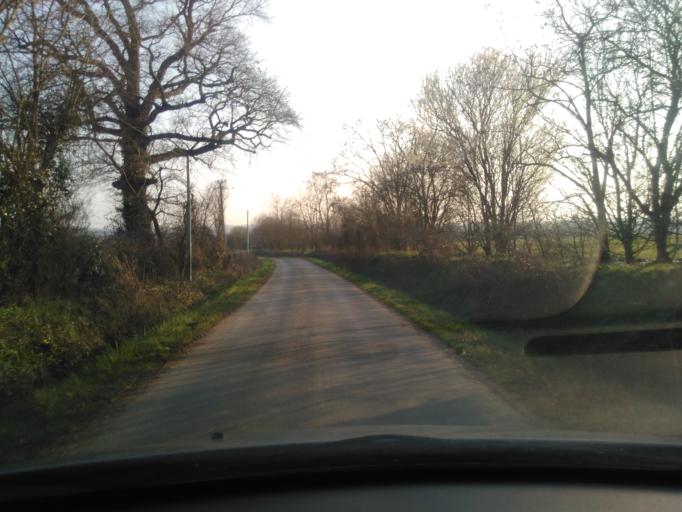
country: FR
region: Pays de la Loire
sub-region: Departement de la Vendee
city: Chantonnay
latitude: 46.6685
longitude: -1.0315
